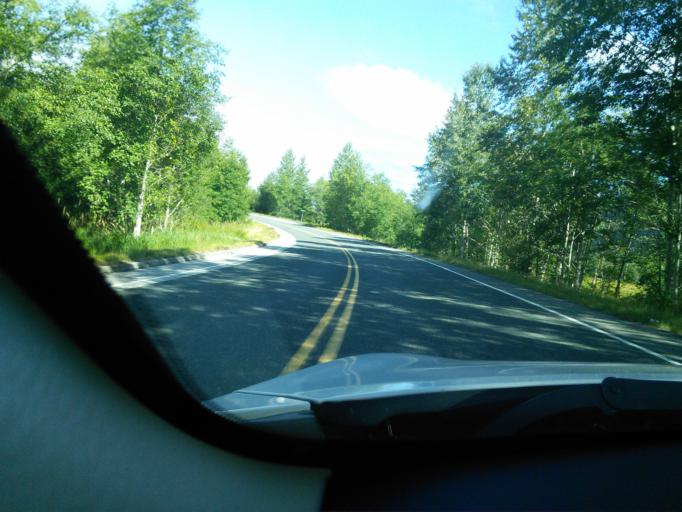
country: CA
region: British Columbia
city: Campbell River
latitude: 50.3595
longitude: -125.9135
